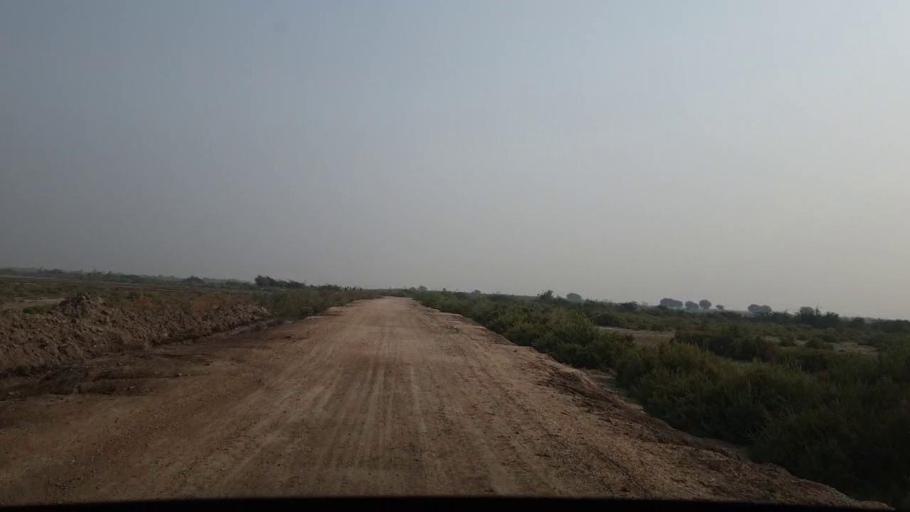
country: PK
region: Sindh
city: Jati
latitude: 24.2807
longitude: 68.4185
